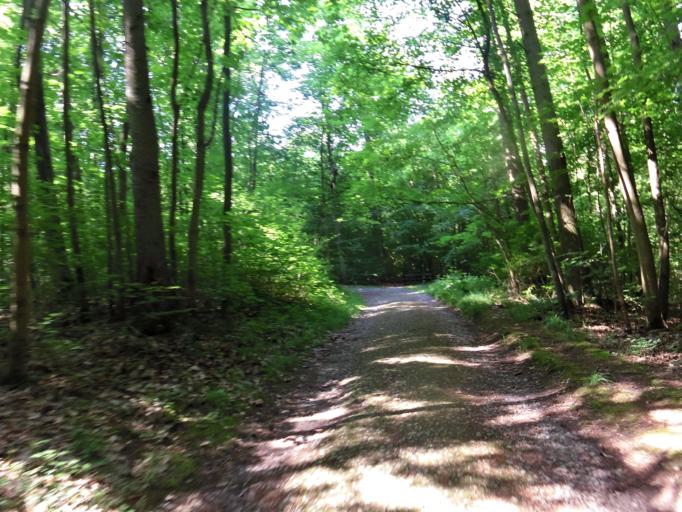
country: DE
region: Bavaria
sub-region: Regierungsbezirk Unterfranken
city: Reichenberg
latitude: 49.7650
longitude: 9.9121
